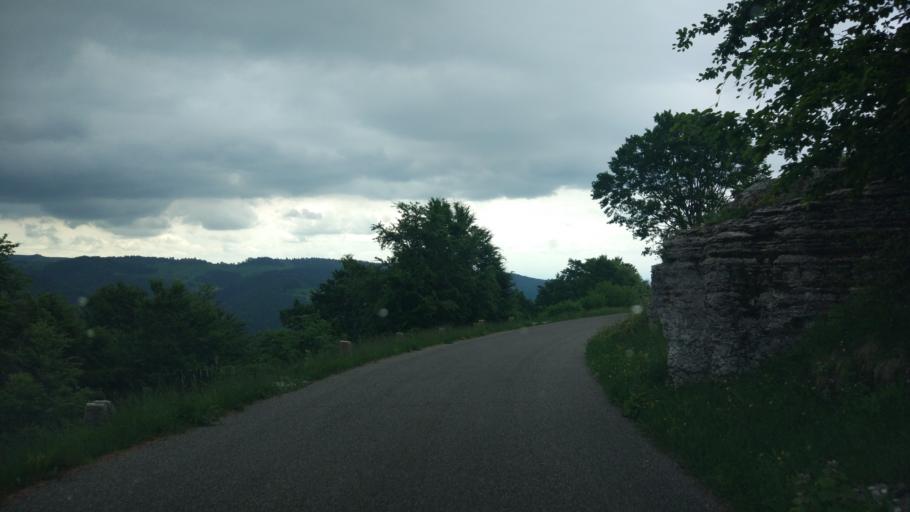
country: IT
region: Veneto
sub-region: Provincia di Verona
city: Erbezzo
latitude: 45.6642
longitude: 11.0002
